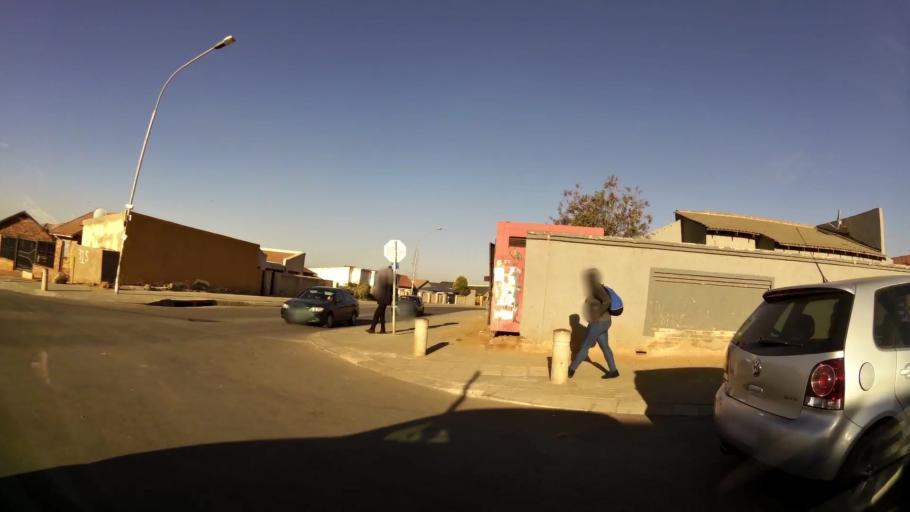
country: ZA
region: Gauteng
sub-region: Ekurhuleni Metropolitan Municipality
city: Tembisa
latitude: -26.0115
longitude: 28.2286
